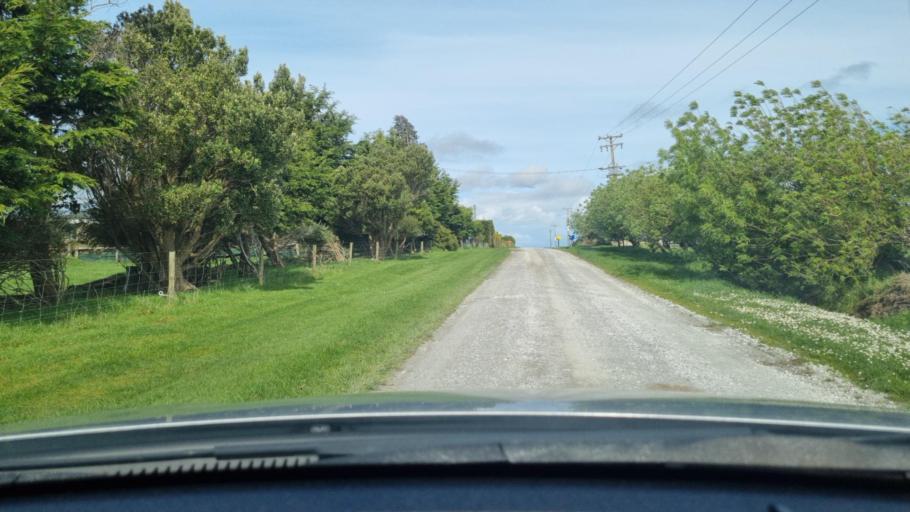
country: NZ
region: Southland
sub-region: Invercargill City
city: Invercargill
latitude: -46.4526
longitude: 168.3824
